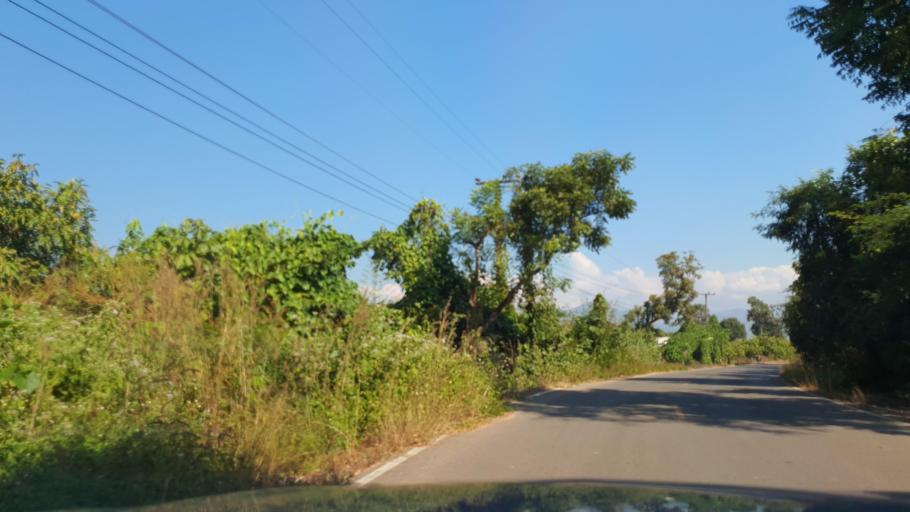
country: TH
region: Nan
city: Pua
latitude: 19.1522
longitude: 100.9103
